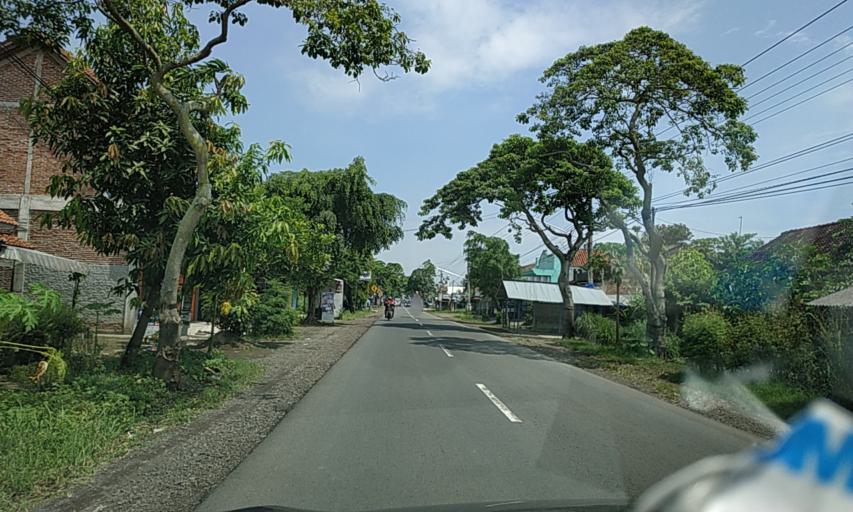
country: ID
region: Central Java
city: Gendiwu
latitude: -7.4863
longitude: 108.8124
